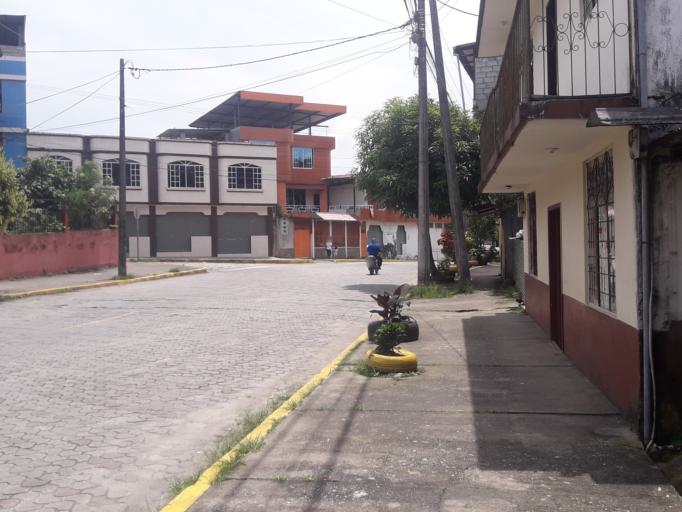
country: EC
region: Napo
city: Tena
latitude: -0.9922
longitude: -77.8127
